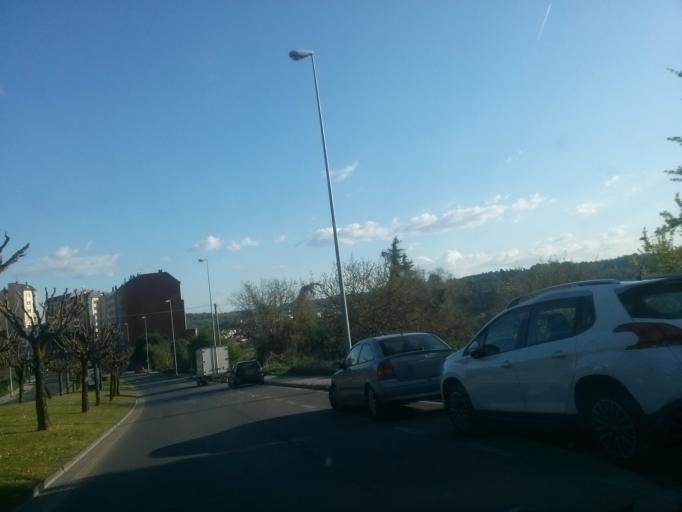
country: ES
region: Galicia
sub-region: Provincia de Lugo
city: Lugo
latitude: 43.0081
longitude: -7.5654
